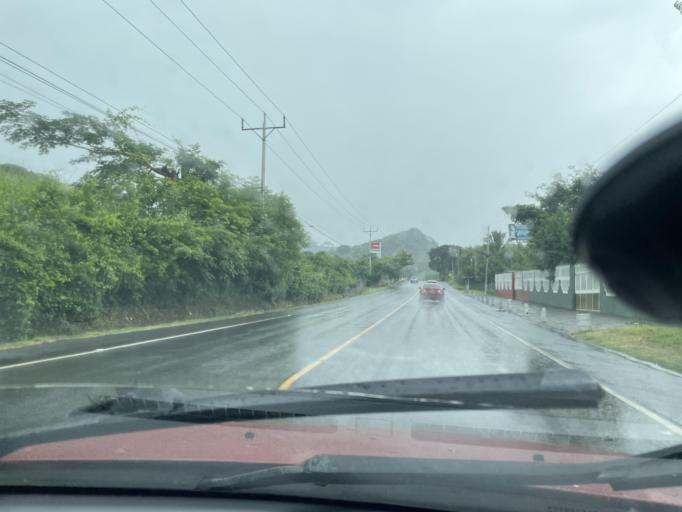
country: SV
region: Morazan
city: Jocoro
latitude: 13.5668
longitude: -88.0933
